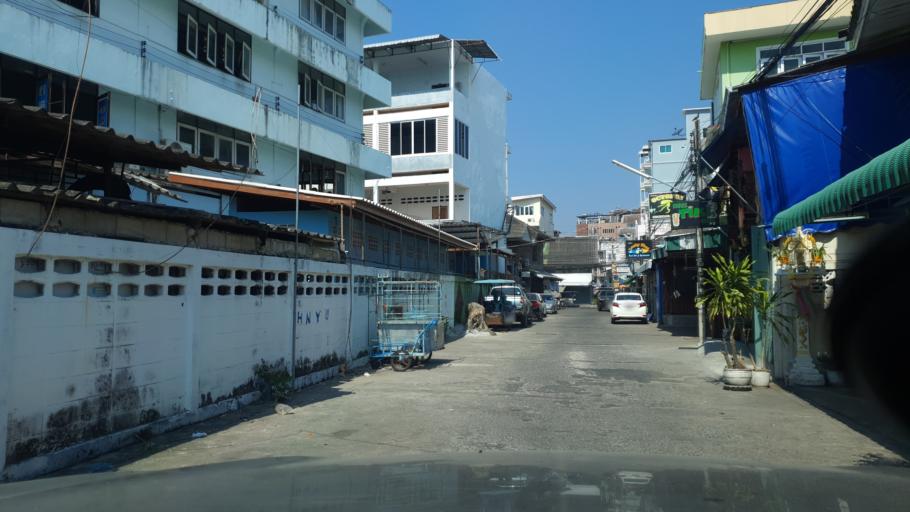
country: TH
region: Prachuap Khiri Khan
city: Hua Hin
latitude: 12.5713
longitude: 99.9582
